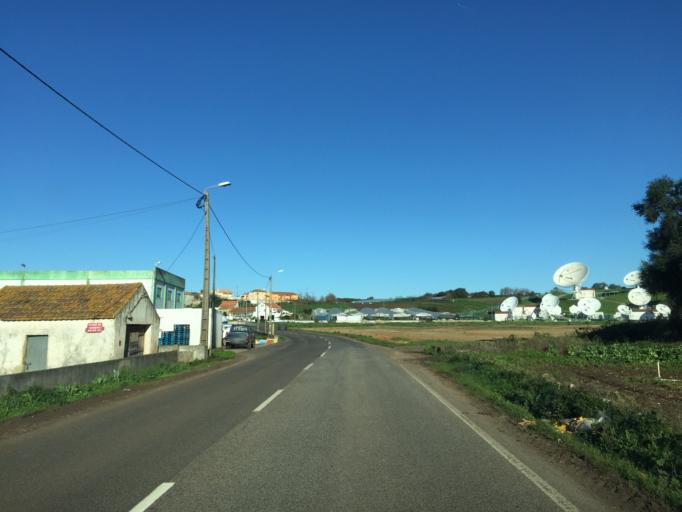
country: PT
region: Lisbon
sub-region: Sintra
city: Almargem
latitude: 38.8653
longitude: -9.2824
